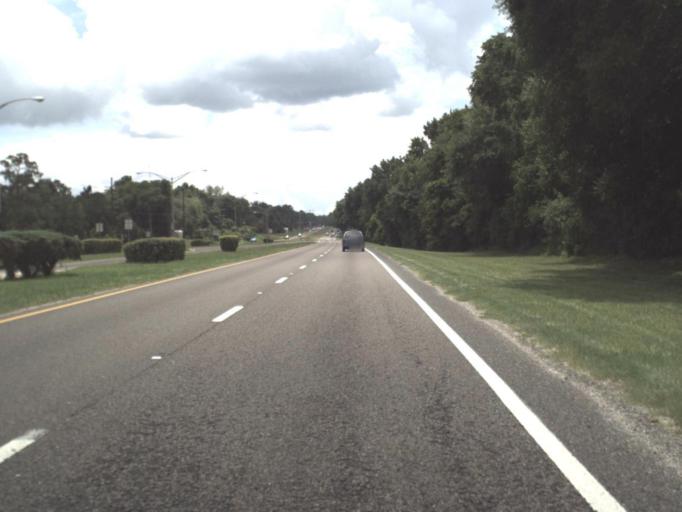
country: US
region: Florida
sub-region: Putnam County
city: East Palatka
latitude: 29.6240
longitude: -81.5868
